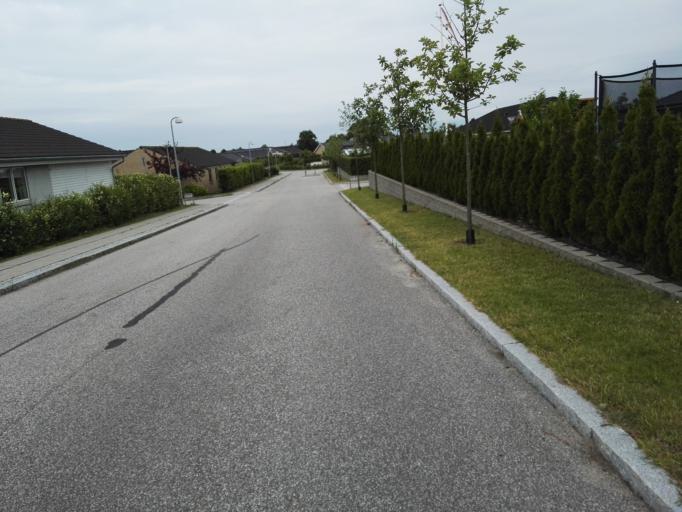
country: DK
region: Capital Region
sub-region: Egedal Kommune
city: Olstykke
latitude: 55.7882
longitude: 12.1501
